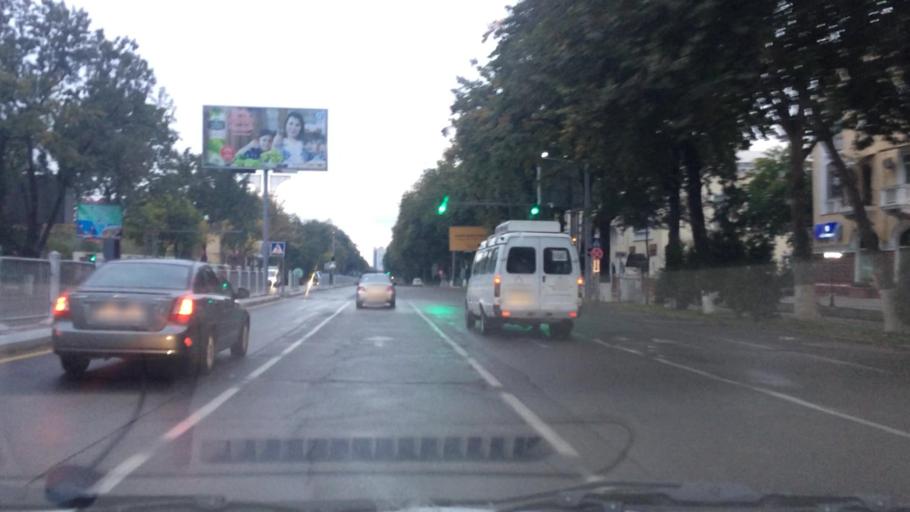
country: UZ
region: Toshkent Shahri
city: Tashkent
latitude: 41.3208
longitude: 69.2618
